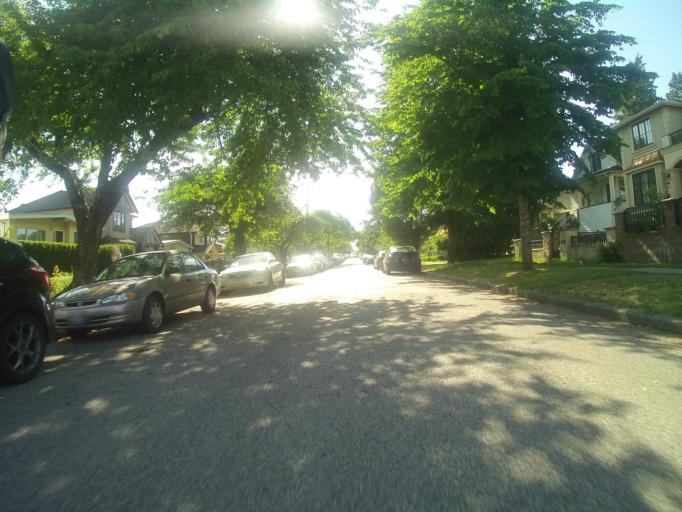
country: CA
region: British Columbia
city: Vancouver
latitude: 49.2167
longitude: -123.0988
